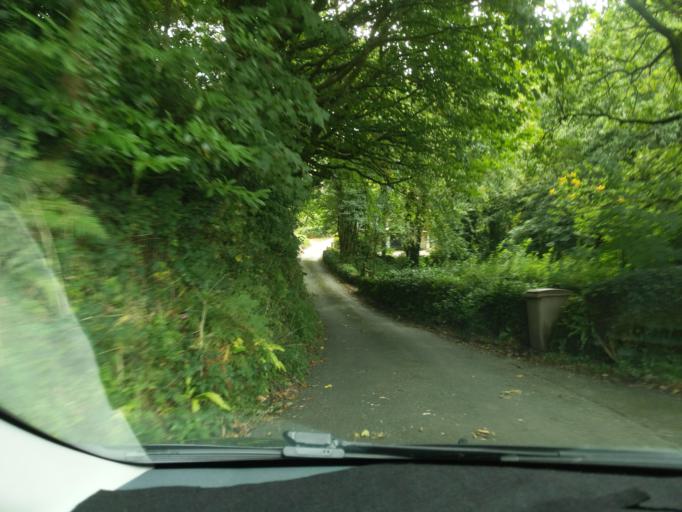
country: GB
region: England
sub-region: Cornwall
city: Lostwithiel
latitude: 50.3961
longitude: -4.7039
